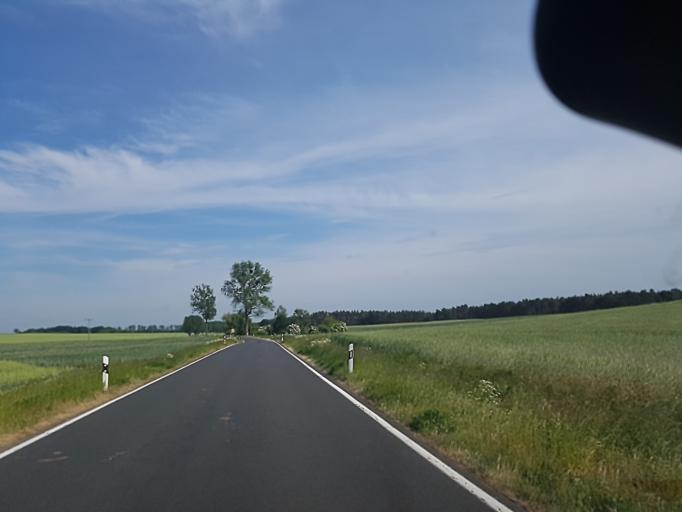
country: DE
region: Saxony-Anhalt
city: Kropstadt
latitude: 51.9770
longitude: 12.7230
